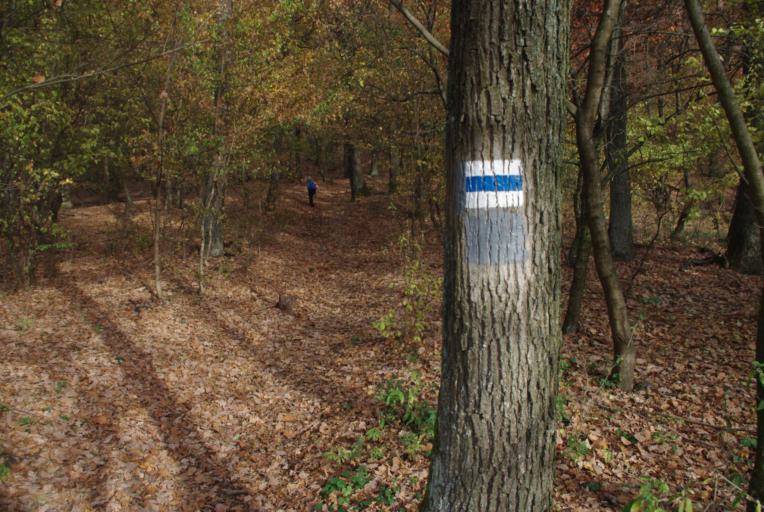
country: HU
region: Borsod-Abauj-Zemplen
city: Satoraljaujhely
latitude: 48.3987
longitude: 21.6102
